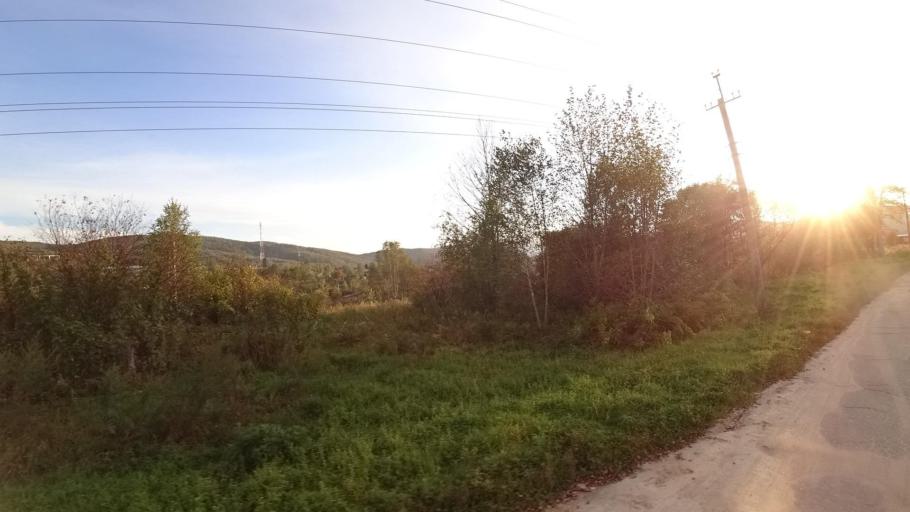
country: RU
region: Jewish Autonomous Oblast
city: Kul'dur
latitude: 49.2081
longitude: 131.6422
